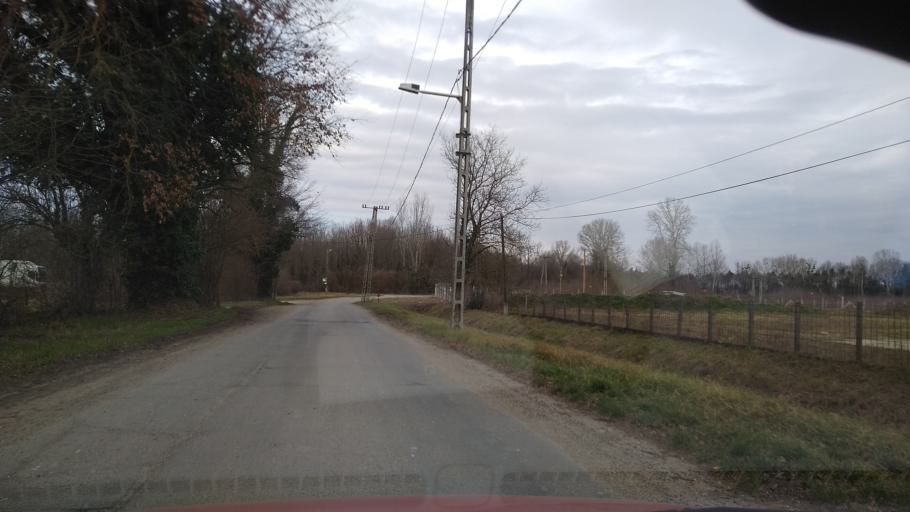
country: HU
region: Somogy
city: Barcs
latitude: 45.9562
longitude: 17.4413
